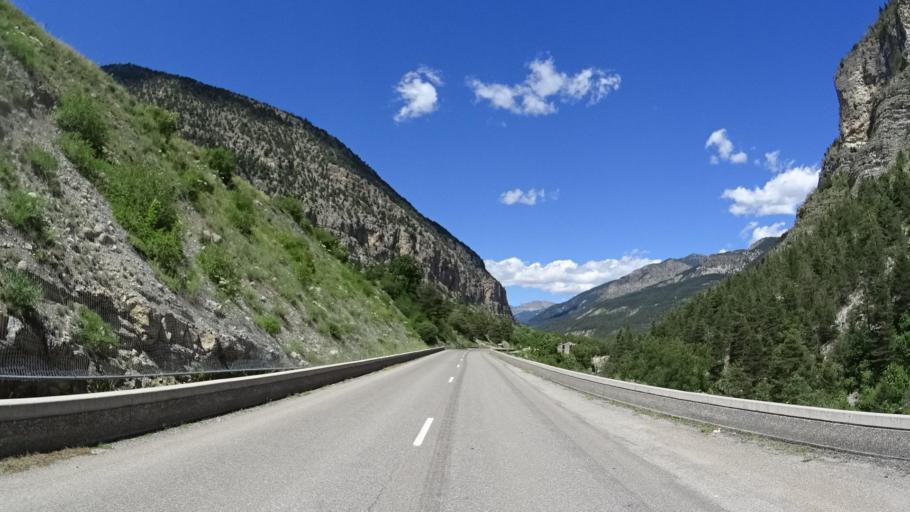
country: FR
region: Provence-Alpes-Cote d'Azur
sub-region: Departement des Alpes-de-Haute-Provence
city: Annot
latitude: 44.0979
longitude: 6.5669
